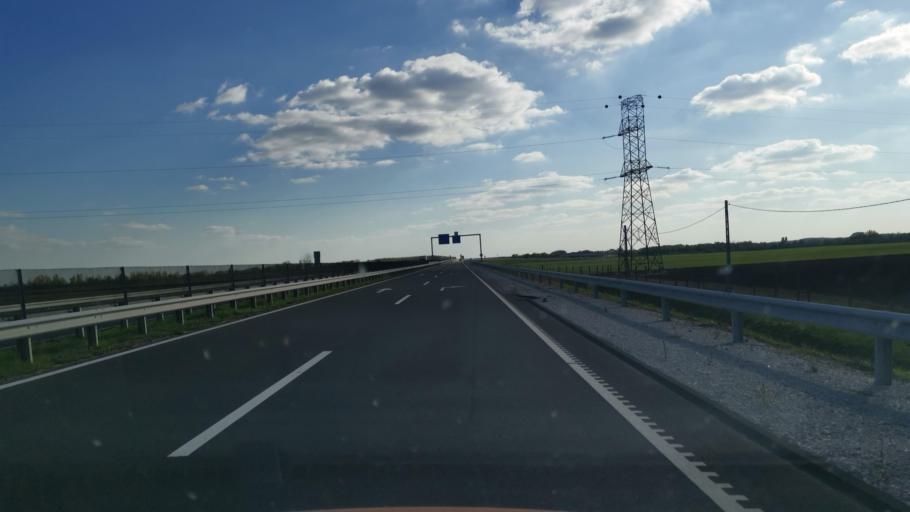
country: HU
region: Heves
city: Erdotelek
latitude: 47.7319
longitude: 20.3414
